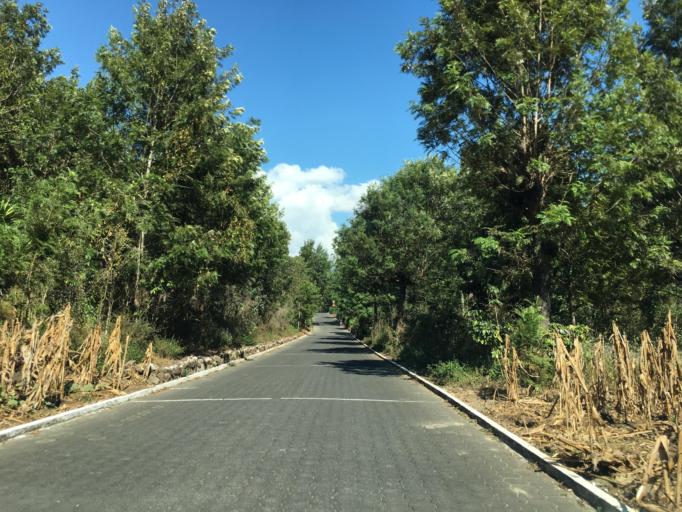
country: GT
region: Solola
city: Santiago Atitlan
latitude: 14.6618
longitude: -91.1754
